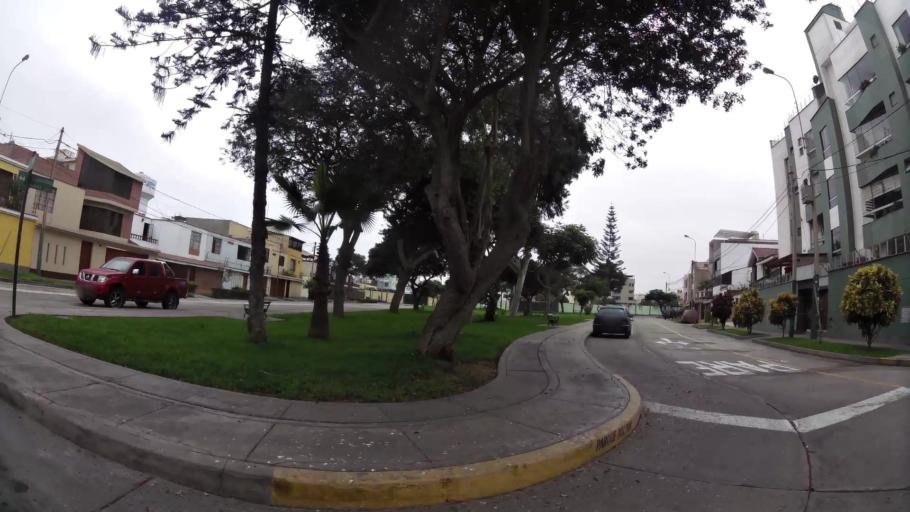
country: PE
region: Lima
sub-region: Lima
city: Surco
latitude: -12.1316
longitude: -76.9899
